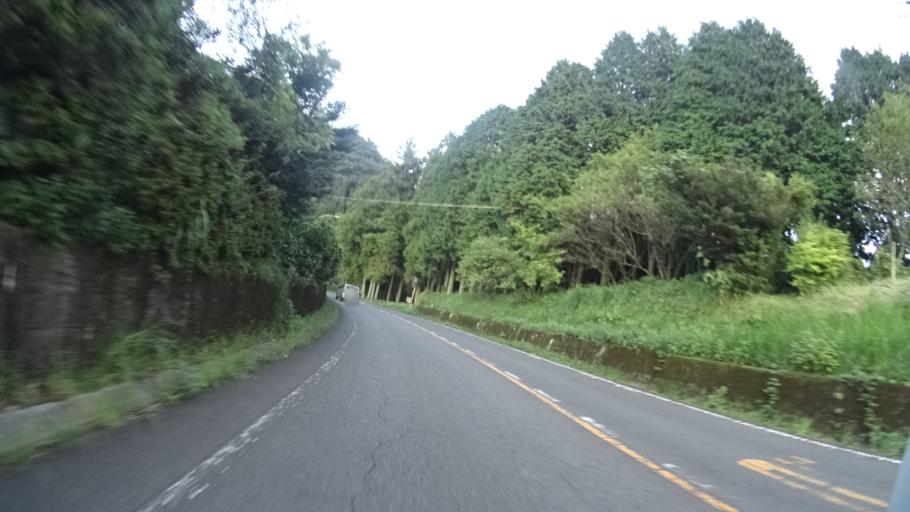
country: JP
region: Oita
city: Beppu
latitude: 33.3349
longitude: 131.4081
